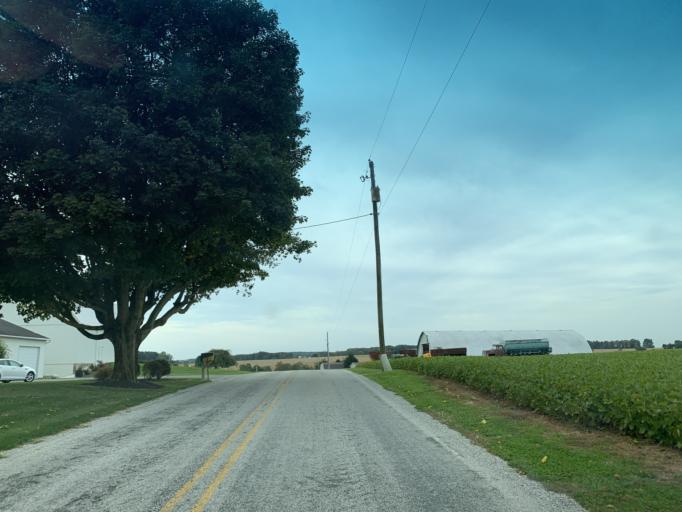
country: US
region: Pennsylvania
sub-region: York County
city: Stewartstown
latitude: 39.8037
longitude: -76.5120
